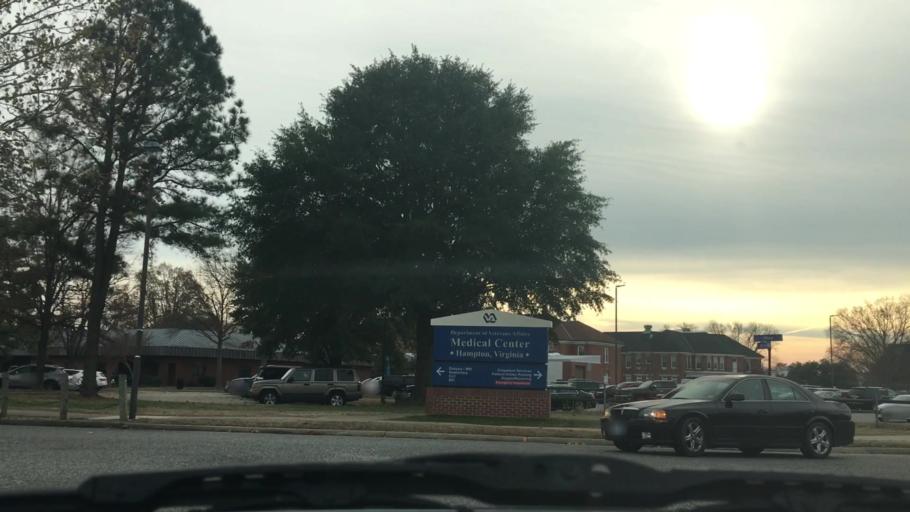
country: US
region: Virginia
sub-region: City of Hampton
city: Hampton
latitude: 37.0185
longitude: -76.3307
